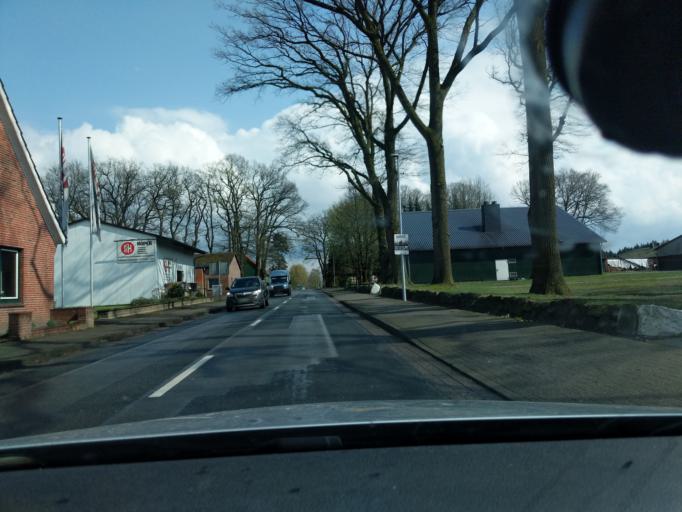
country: DE
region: Lower Saxony
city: Bargstedt
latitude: 53.4646
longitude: 9.4728
